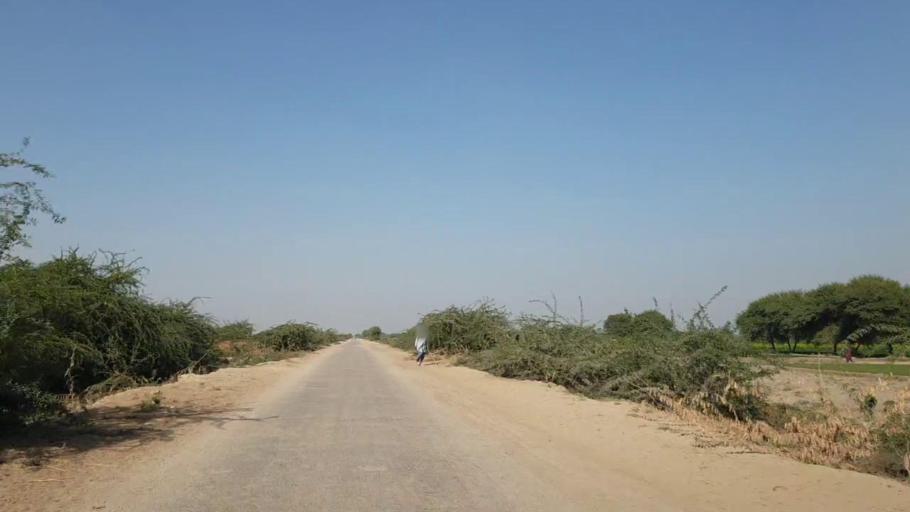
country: PK
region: Sindh
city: Digri
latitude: 25.0092
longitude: 69.1062
